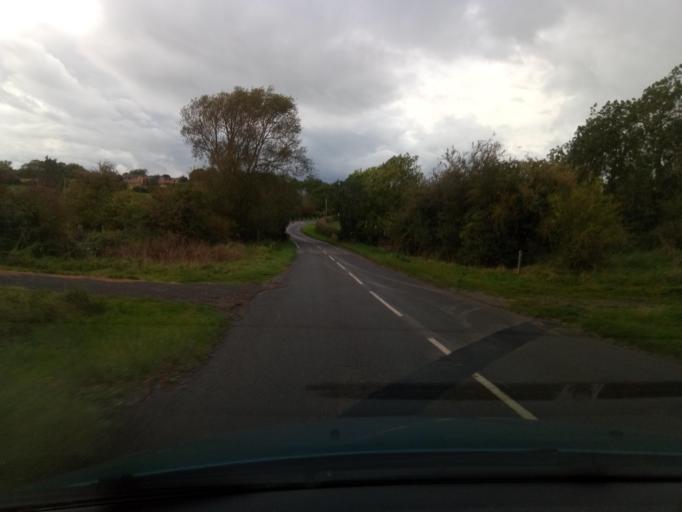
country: GB
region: England
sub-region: Leicestershire
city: Sileby
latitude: 52.7497
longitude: -1.0783
